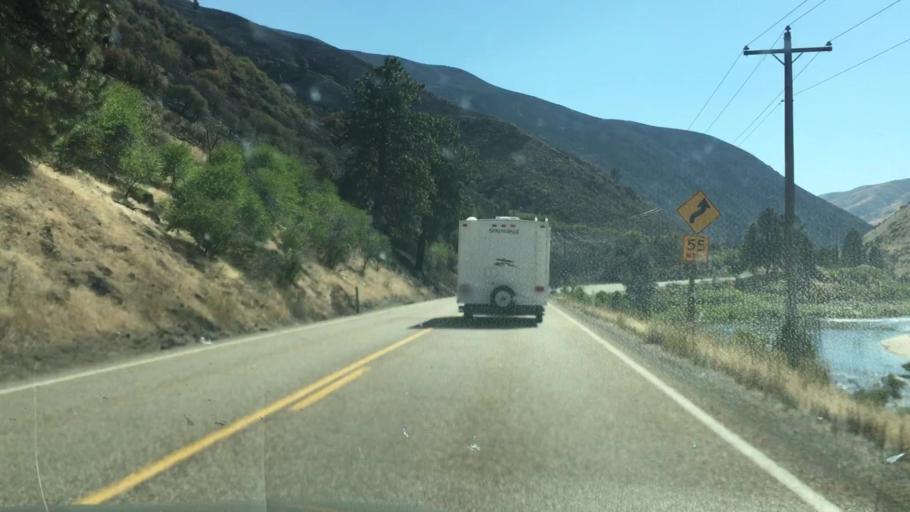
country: US
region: Idaho
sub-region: Boise County
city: Idaho City
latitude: 44.0161
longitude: -116.1533
